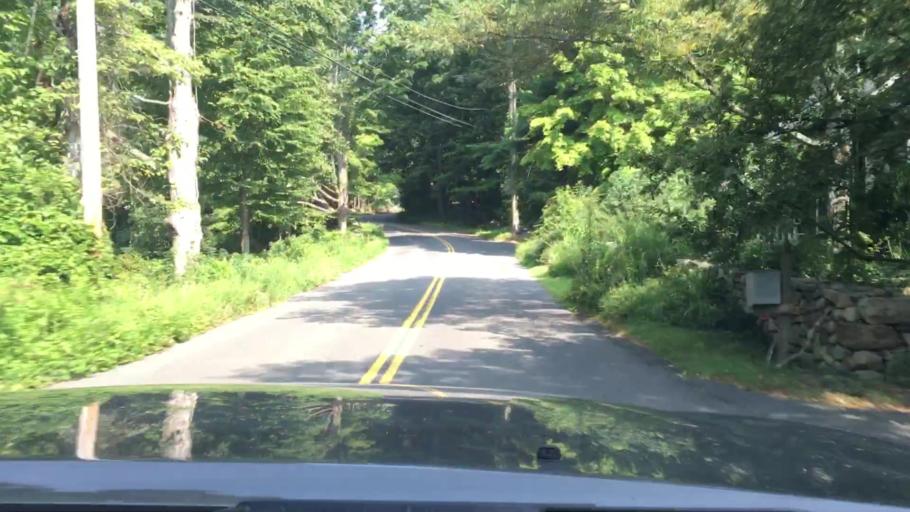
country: US
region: Connecticut
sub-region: Fairfield County
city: Georgetown
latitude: 41.2536
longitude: -73.4551
